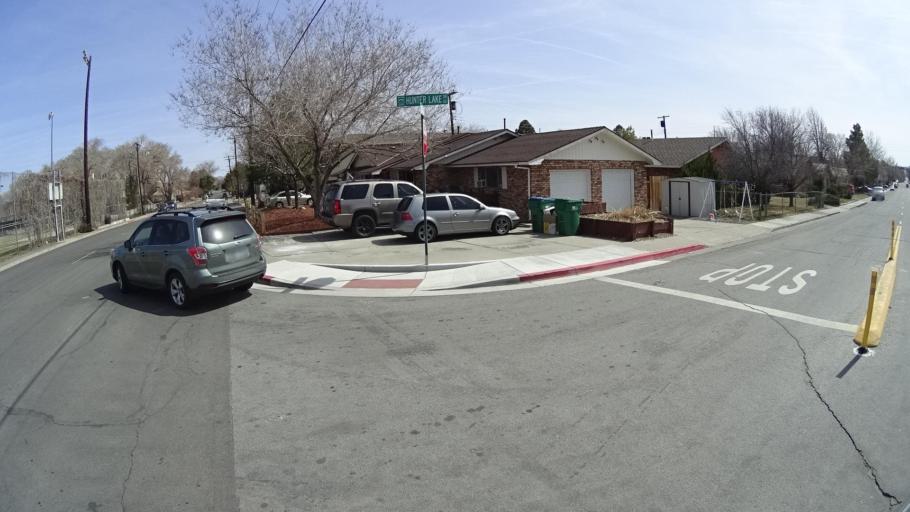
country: US
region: Nevada
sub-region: Washoe County
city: Reno
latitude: 39.5196
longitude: -119.8358
